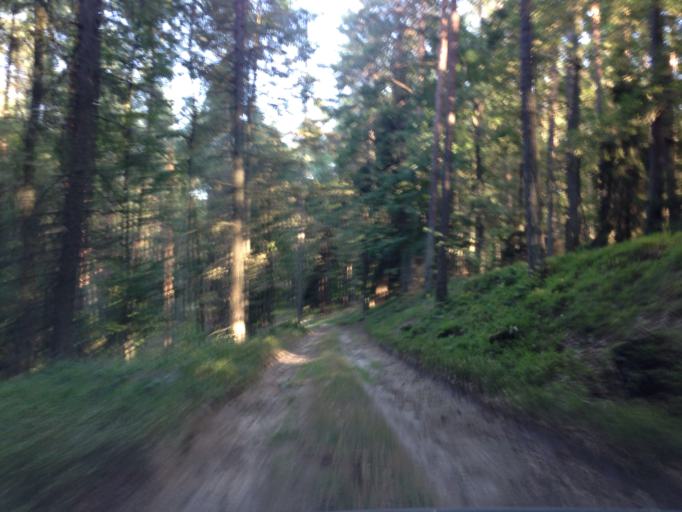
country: PL
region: Kujawsko-Pomorskie
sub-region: Powiat brodnicki
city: Gorzno
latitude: 53.1941
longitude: 19.7282
